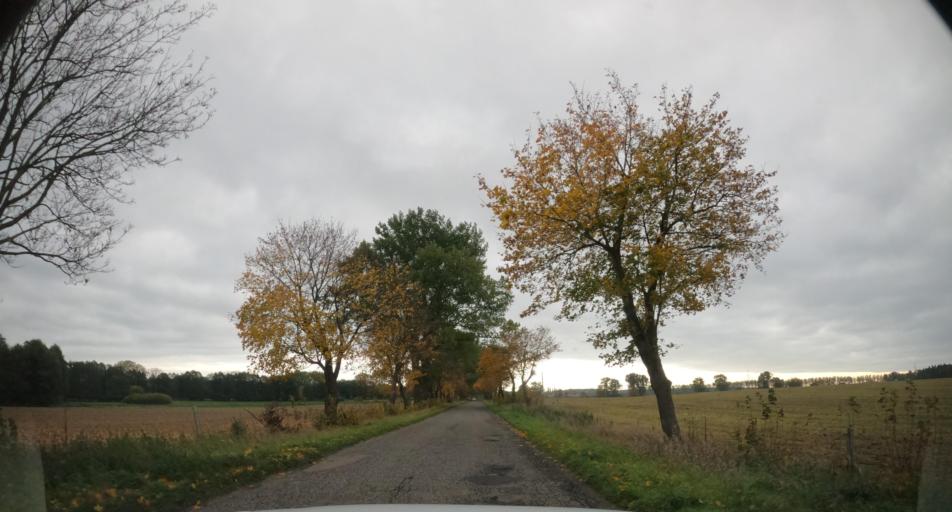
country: PL
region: West Pomeranian Voivodeship
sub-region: Powiat kamienski
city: Wolin
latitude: 53.8630
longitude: 14.5938
